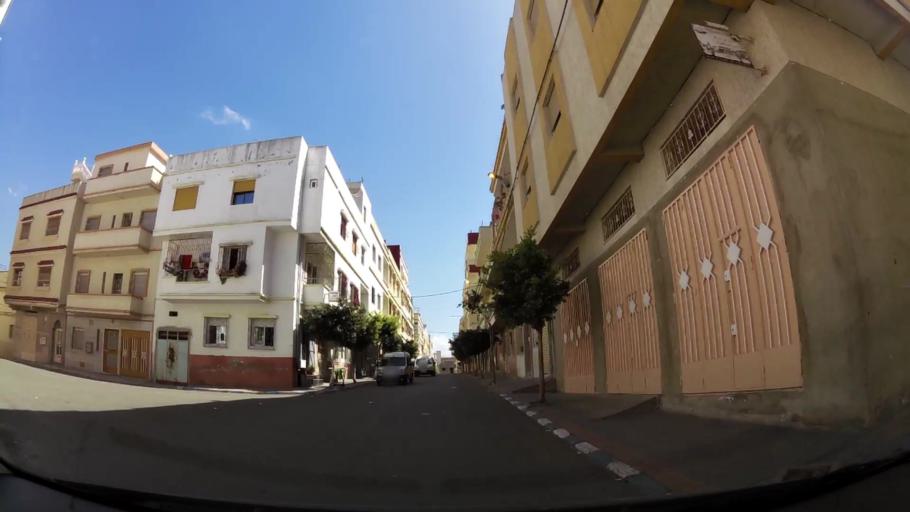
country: MA
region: Tanger-Tetouan
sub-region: Tanger-Assilah
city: Tangier
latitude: 35.7514
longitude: -5.8117
